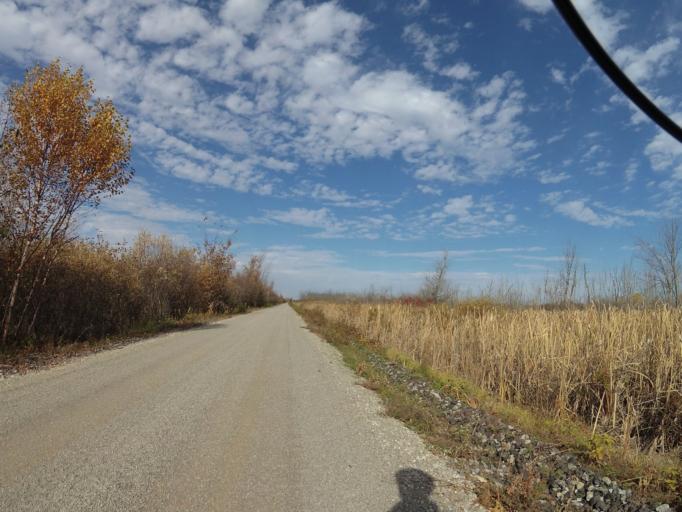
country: CA
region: Ontario
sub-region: Lanark County
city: Smiths Falls
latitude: 45.0188
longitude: -76.0743
